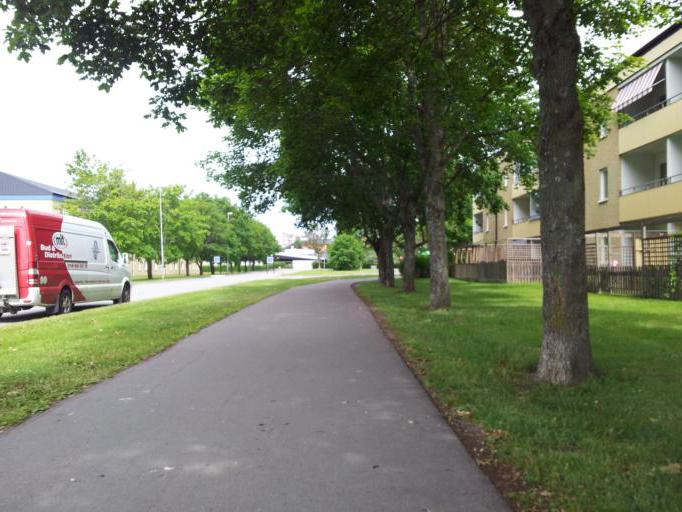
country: SE
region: Uppsala
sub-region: Uppsala Kommun
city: Gamla Uppsala
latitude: 59.8861
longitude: 17.6565
